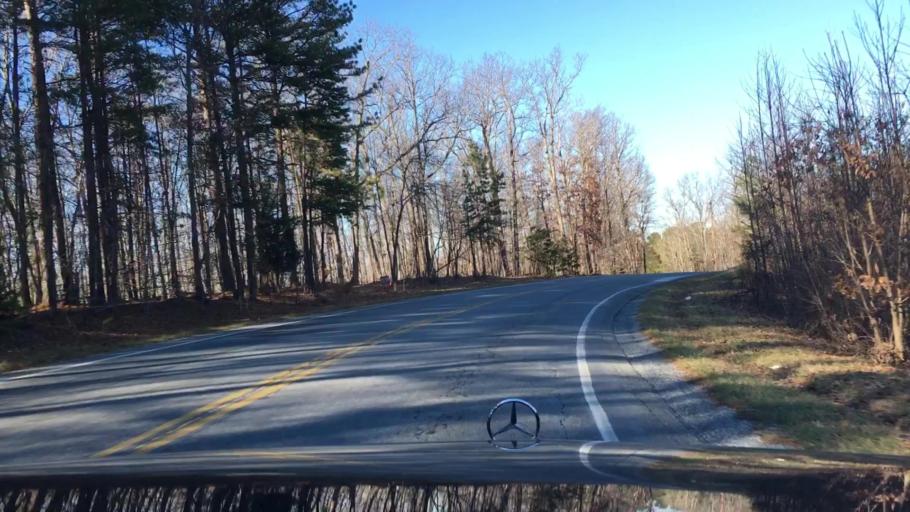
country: US
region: Virginia
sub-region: Pittsylvania County
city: Motley
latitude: 37.1666
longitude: -79.4053
